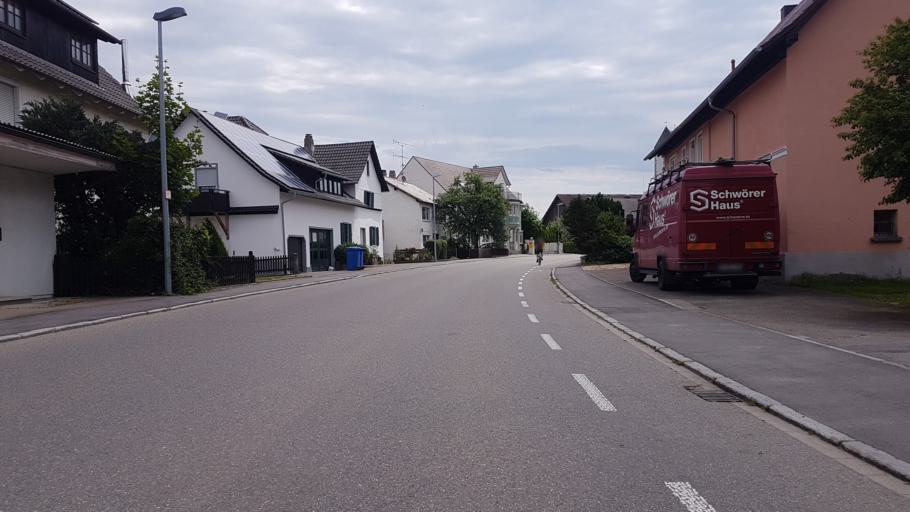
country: DE
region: Baden-Wuerttemberg
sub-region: Tuebingen Region
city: Ennetach
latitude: 48.0548
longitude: 9.3177
